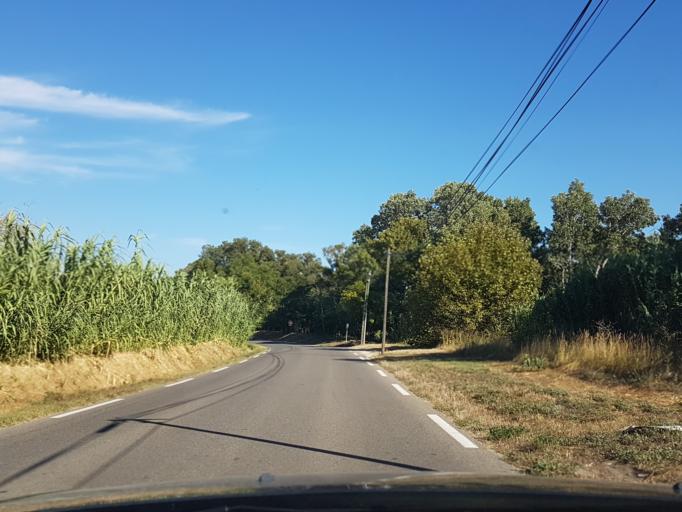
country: FR
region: Provence-Alpes-Cote d'Azur
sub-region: Departement du Vaucluse
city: Monteux
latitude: 44.0395
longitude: 4.9800
